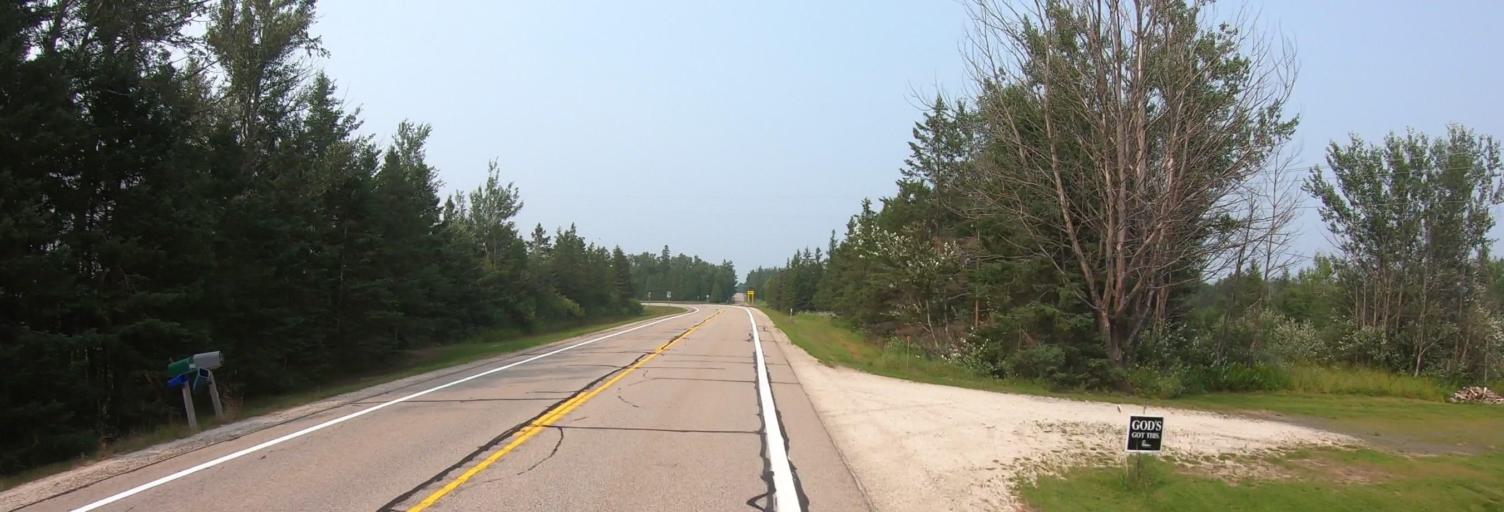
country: US
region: Michigan
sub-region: Chippewa County
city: Sault Ste. Marie
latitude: 46.1257
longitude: -84.2595
